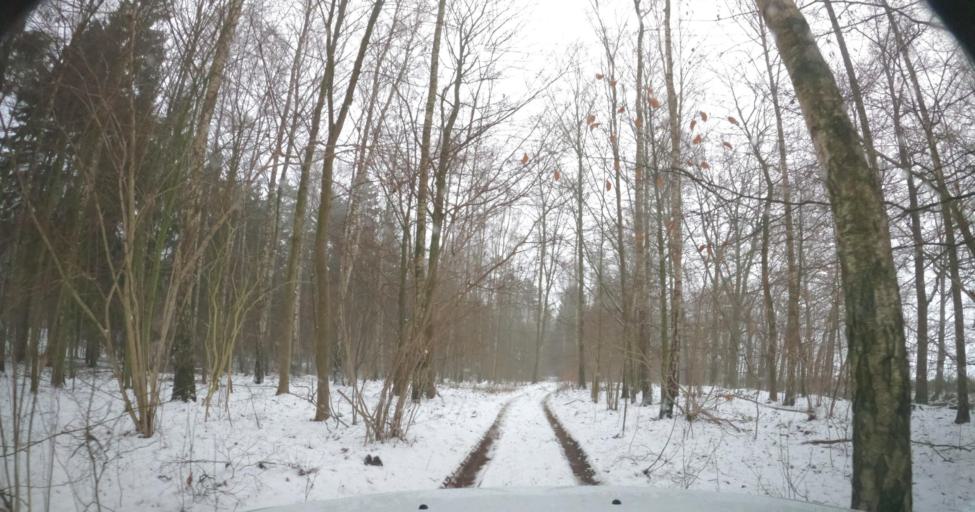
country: PL
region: West Pomeranian Voivodeship
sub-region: Powiat kamienski
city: Golczewo
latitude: 53.8703
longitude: 15.0398
